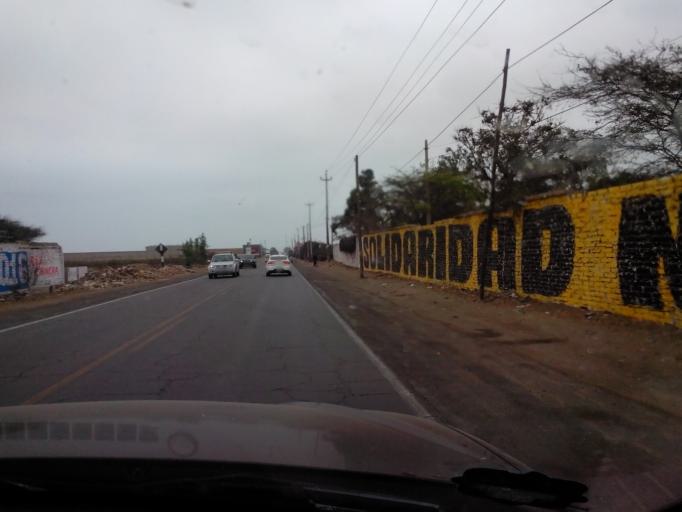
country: PE
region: Ica
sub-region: Provincia de Chincha
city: San Pedro
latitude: -13.4097
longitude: -76.1698
